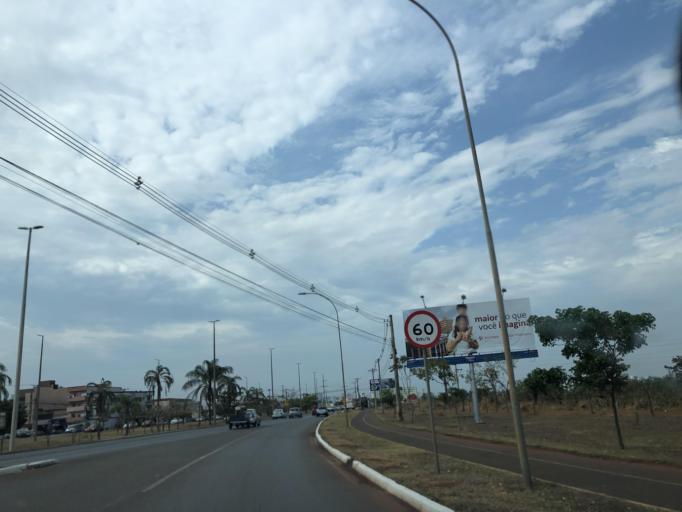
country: BR
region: Federal District
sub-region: Brasilia
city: Brasilia
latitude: -15.8708
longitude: -48.0565
